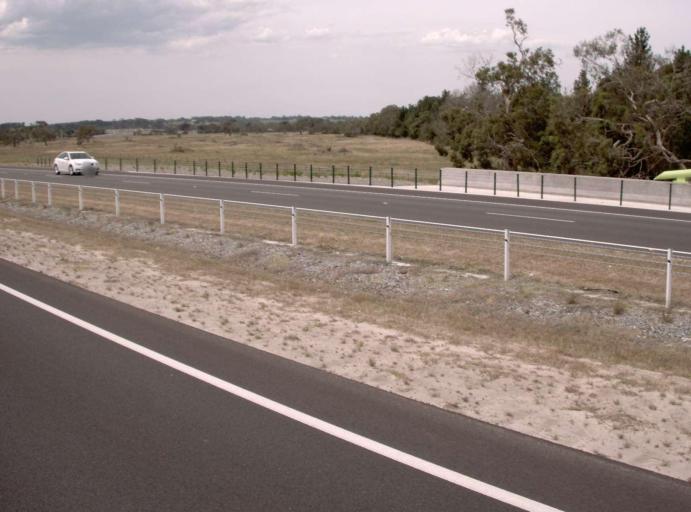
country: AU
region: Victoria
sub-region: Mornington Peninsula
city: Moorooduc
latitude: -38.2078
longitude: 145.1319
